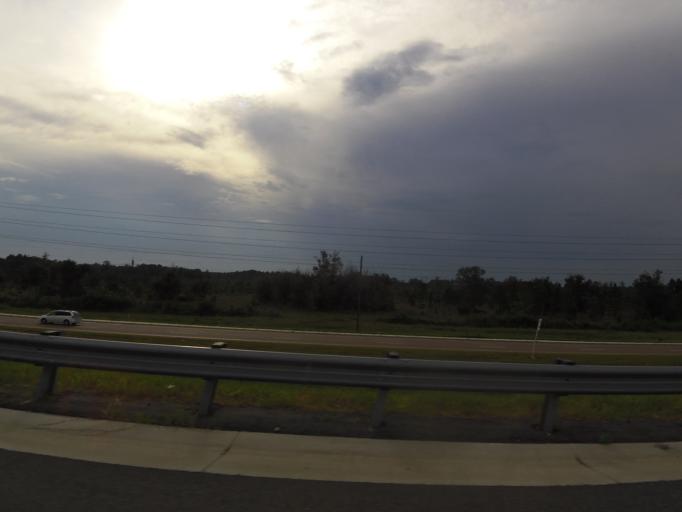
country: US
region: Florida
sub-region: Clay County
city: Middleburg
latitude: 30.1166
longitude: -81.8316
